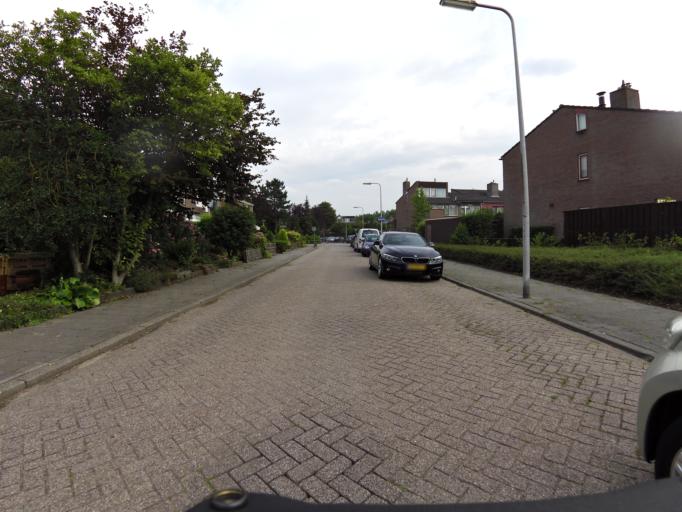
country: NL
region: South Holland
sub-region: Gemeente Maassluis
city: Maassluis
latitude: 51.8832
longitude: 4.2163
